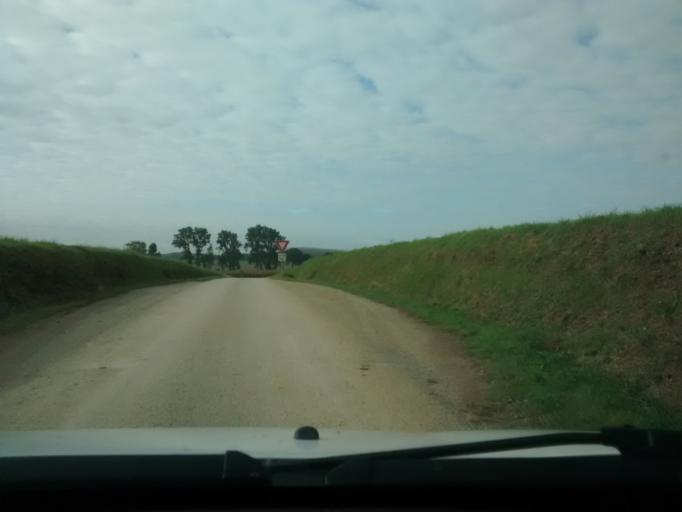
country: FR
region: Brittany
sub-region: Departement d'Ille-et-Vilaine
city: Chavagne
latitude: 48.0789
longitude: -1.7676
